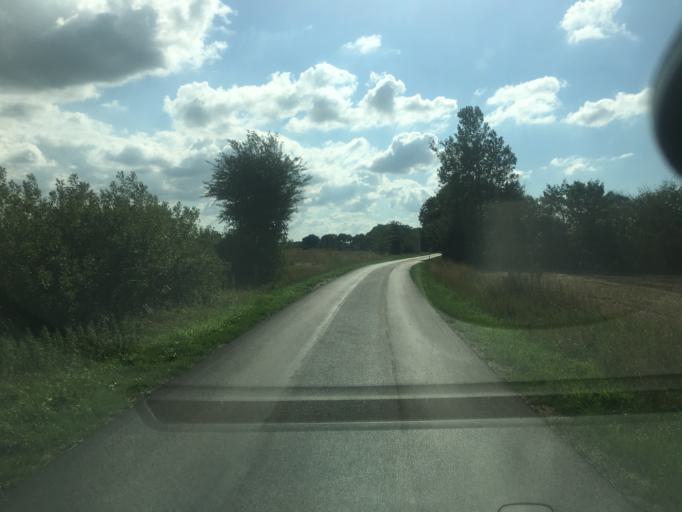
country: DK
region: South Denmark
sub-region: Tonder Kommune
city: Logumkloster
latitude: 54.9842
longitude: 8.9959
